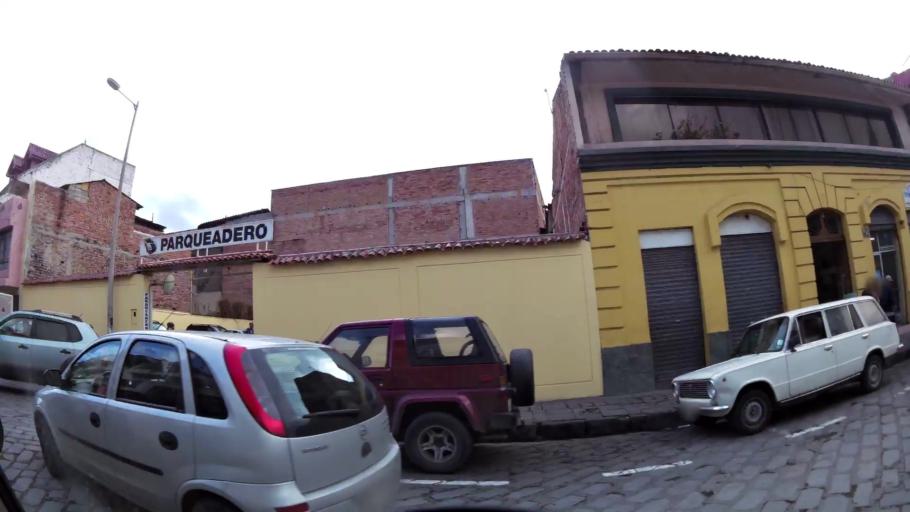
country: EC
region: Azuay
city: Cuenca
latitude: -2.8978
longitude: -78.9989
